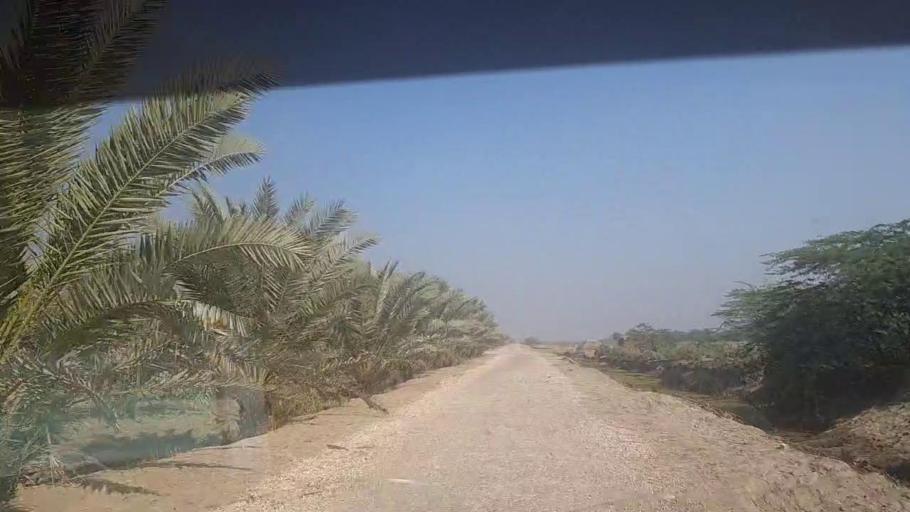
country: PK
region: Sindh
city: Khairpur
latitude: 27.4614
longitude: 68.7297
